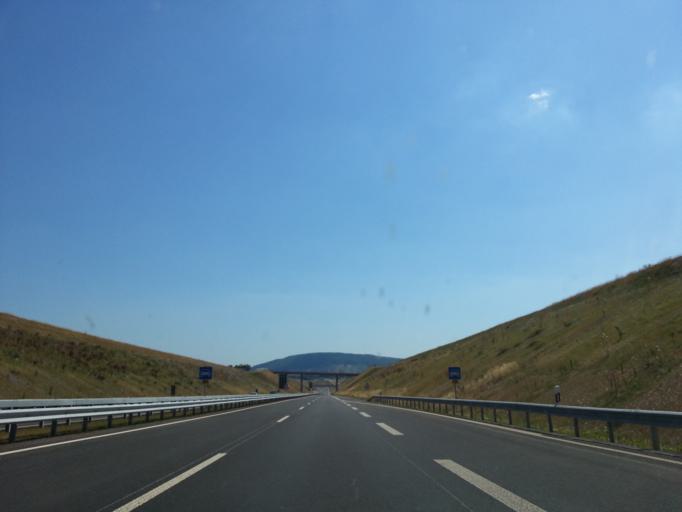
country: DE
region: Rheinland-Pfalz
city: Altrich
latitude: 49.9477
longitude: 6.8934
